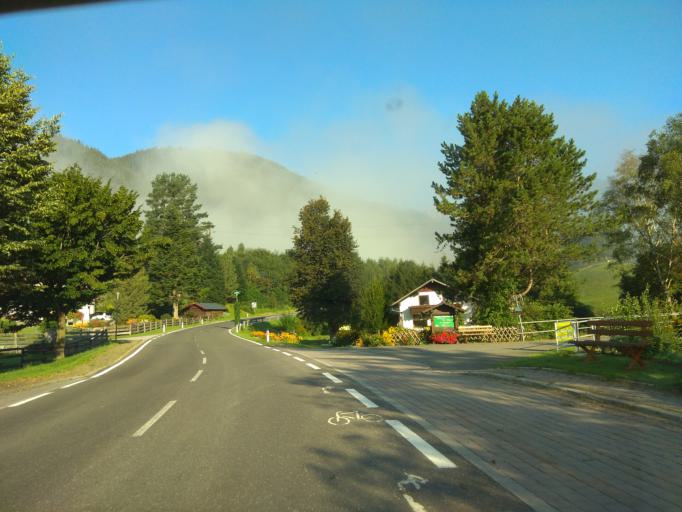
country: AT
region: Styria
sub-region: Politischer Bezirk Leoben
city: Vordernberg
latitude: 47.4985
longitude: 15.0788
